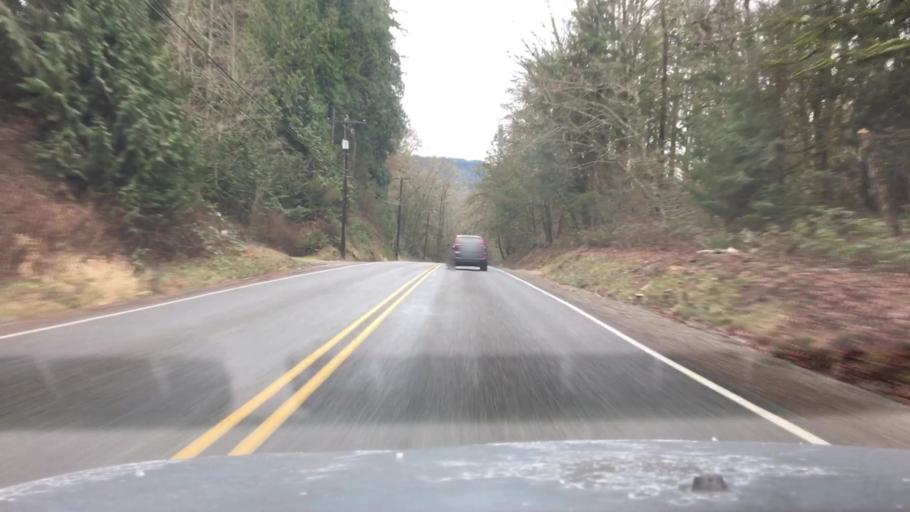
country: US
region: Washington
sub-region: Whatcom County
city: Sudden Valley
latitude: 48.6210
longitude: -122.3299
